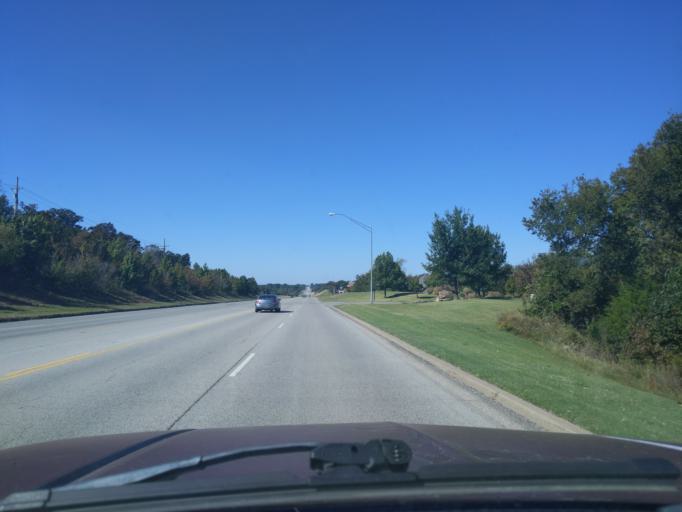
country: US
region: Oklahoma
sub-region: Creek County
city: Kiefer
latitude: 35.9885
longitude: -96.0518
